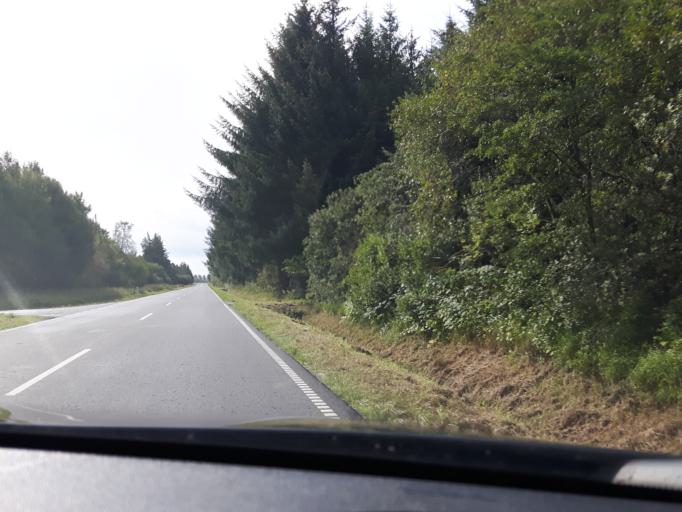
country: DK
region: North Denmark
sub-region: Jammerbugt Kommune
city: Brovst
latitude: 57.1600
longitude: 9.5756
